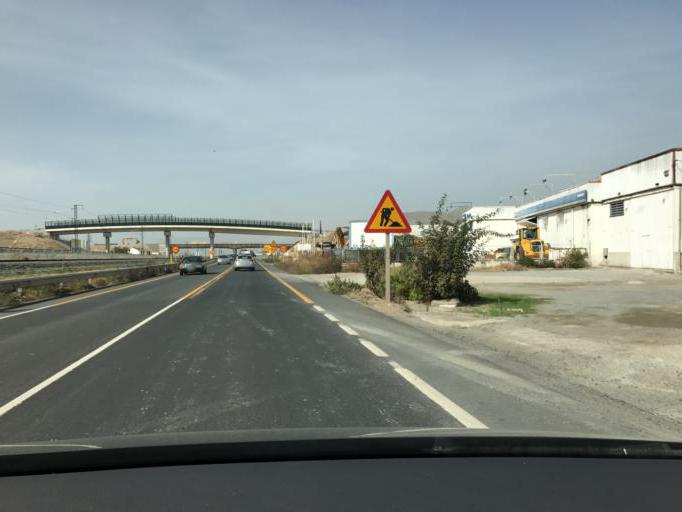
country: ES
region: Andalusia
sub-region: Provincia de Granada
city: Atarfe
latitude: 37.2062
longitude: -3.6707
